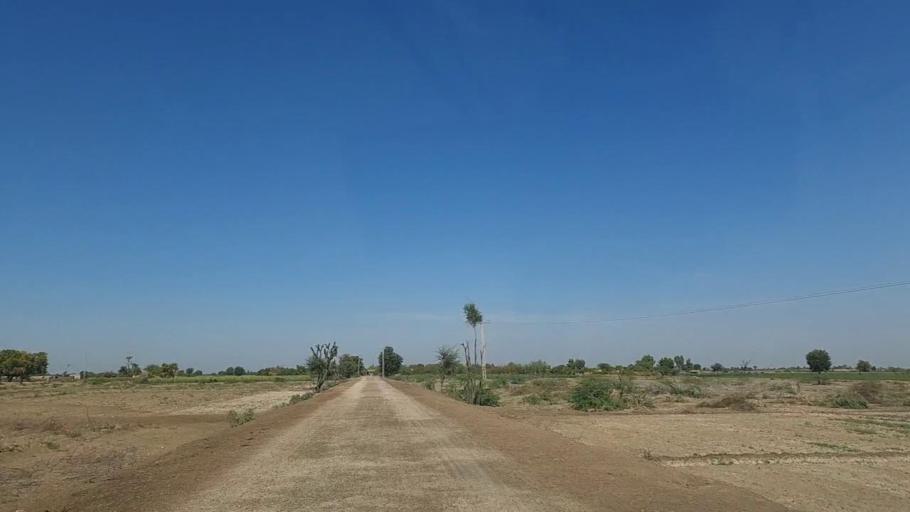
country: PK
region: Sindh
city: Samaro
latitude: 25.3037
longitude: 69.5019
